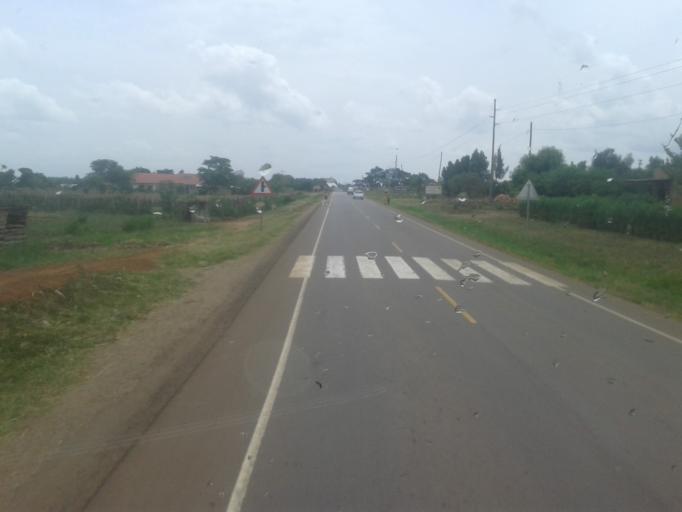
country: UG
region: Western Region
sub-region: Kiryandongo District
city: Kiryandongo
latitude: 1.7834
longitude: 32.0170
